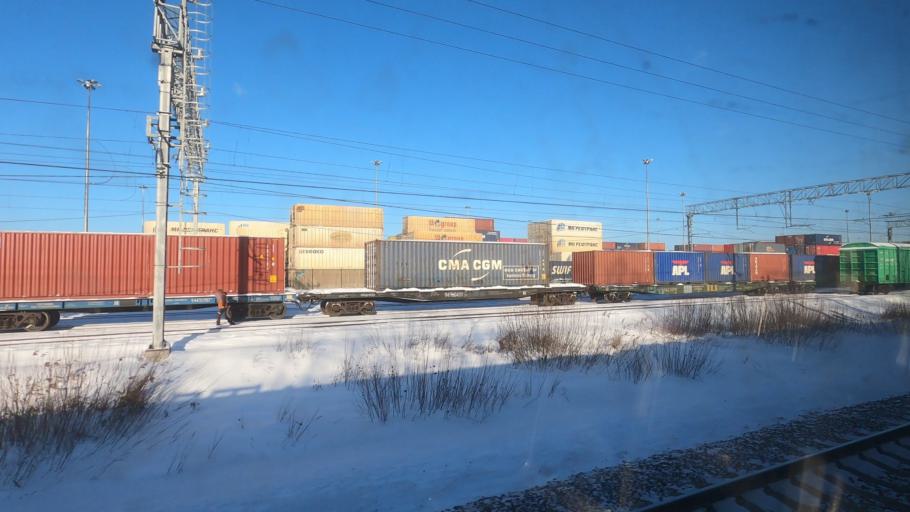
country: RU
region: Moskovskaya
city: Elektrougli
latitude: 55.7234
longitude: 38.2335
